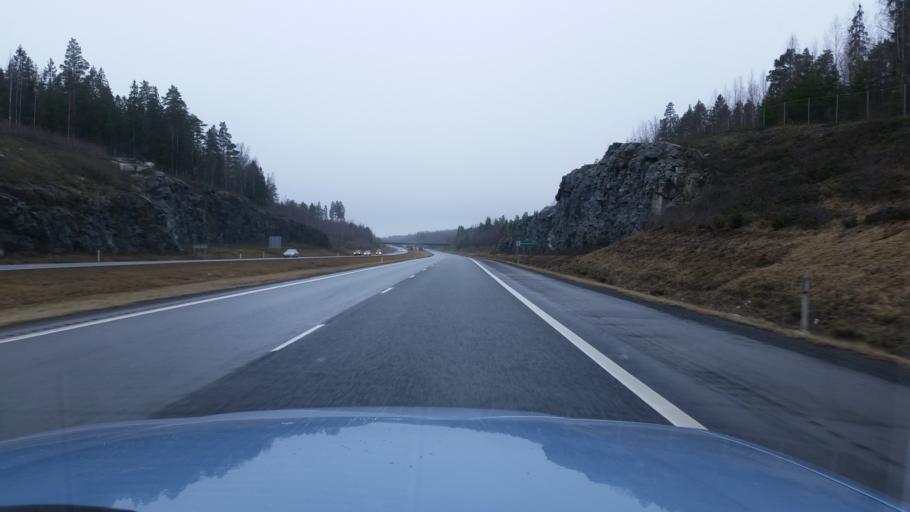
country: FI
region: Pirkanmaa
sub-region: Etelae-Pirkanmaa
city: Toijala
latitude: 61.2425
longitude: 23.8376
